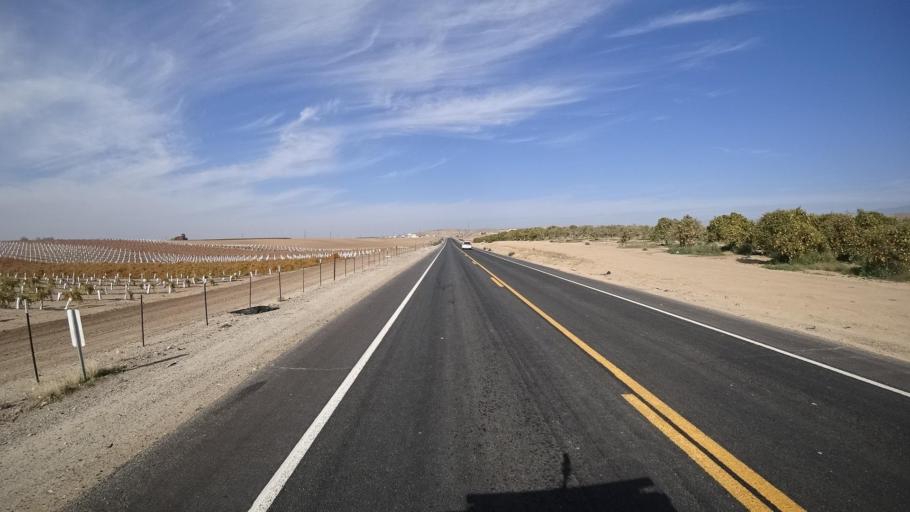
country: US
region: California
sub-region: Kern County
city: Lamont
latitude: 35.3653
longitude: -118.8433
